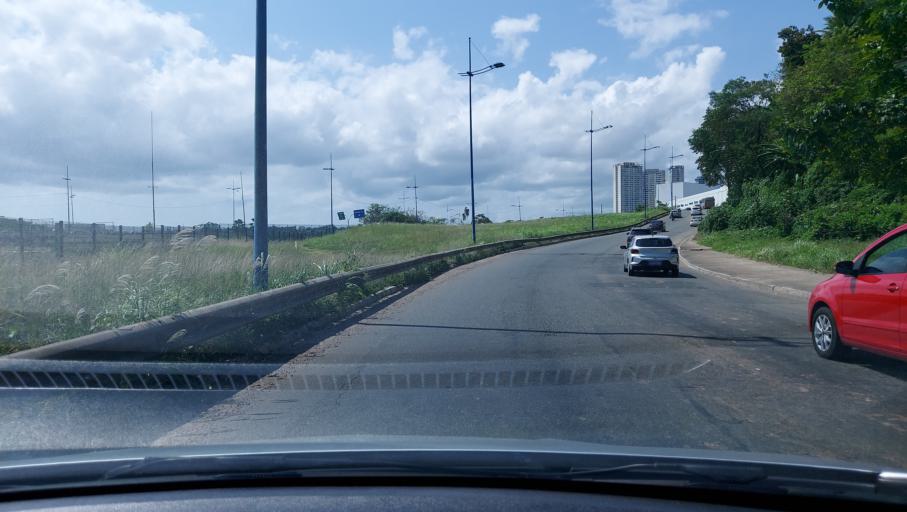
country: BR
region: Bahia
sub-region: Salvador
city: Salvador
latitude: -12.9756
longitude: -38.4755
